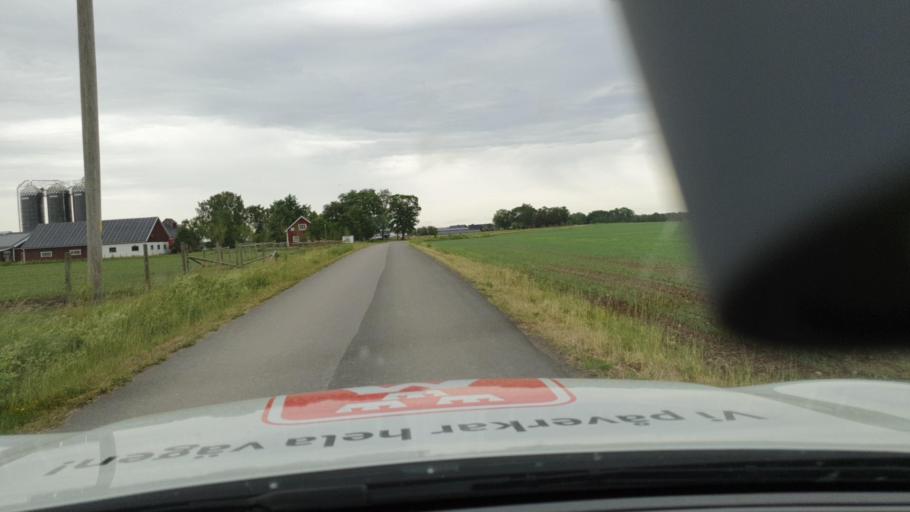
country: SE
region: Vaestra Goetaland
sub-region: Skovde Kommun
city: Skoevde
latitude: 58.3799
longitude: 13.8951
